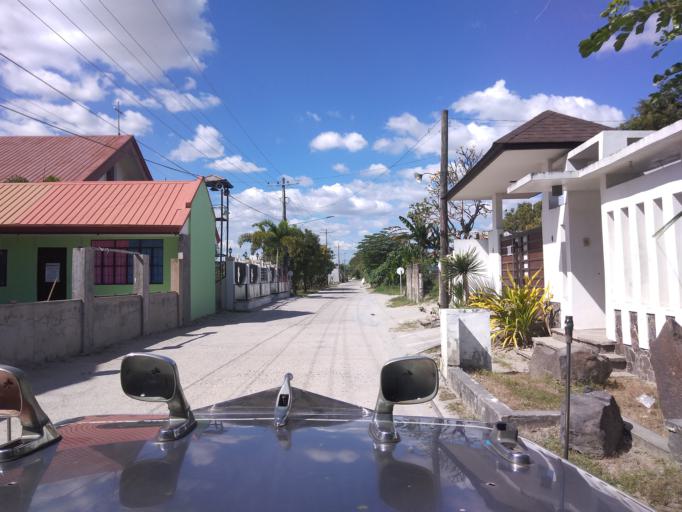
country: PH
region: Central Luzon
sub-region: Province of Pampanga
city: Bacolor
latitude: 15.0114
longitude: 120.6437
